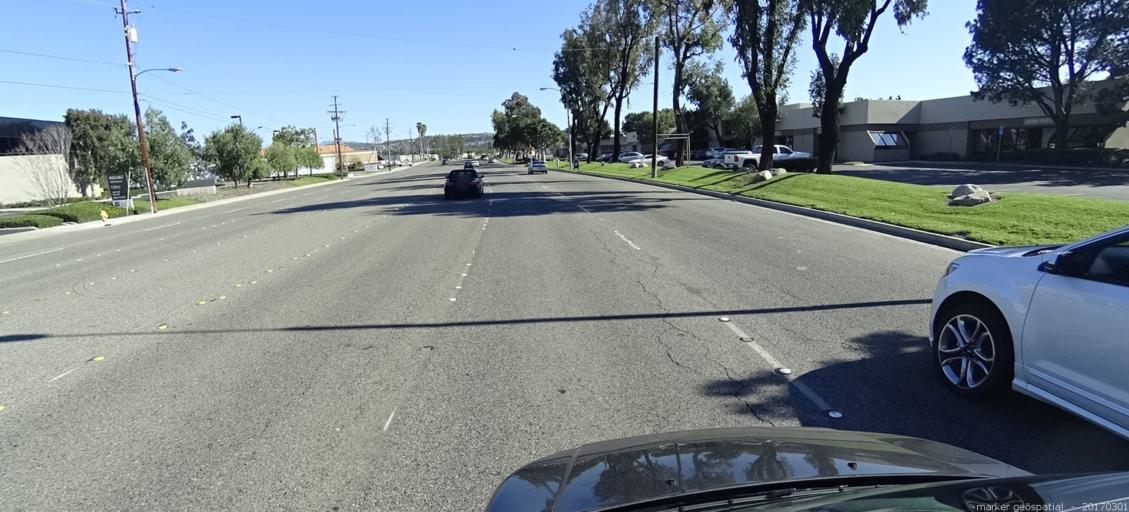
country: US
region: California
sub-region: Orange County
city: Placentia
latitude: 33.8613
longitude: -117.8414
